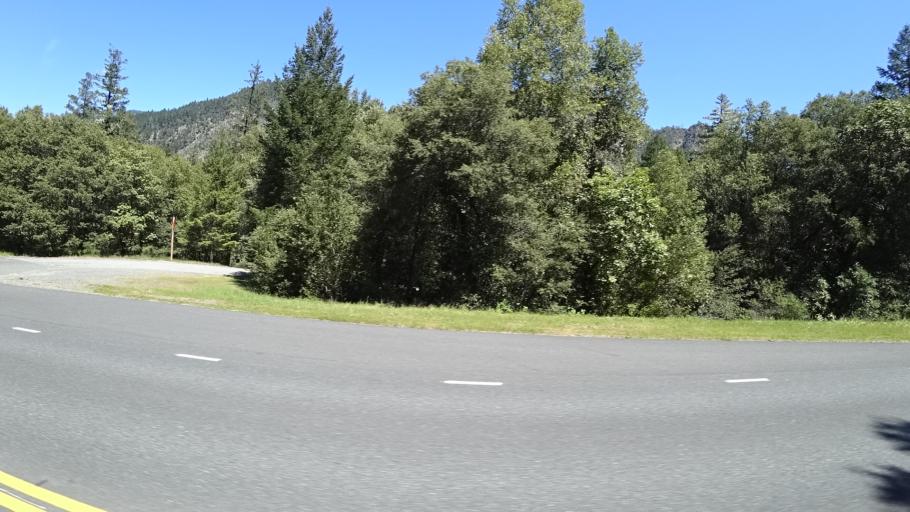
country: US
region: California
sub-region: Humboldt County
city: Willow Creek
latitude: 40.8552
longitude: -123.4927
